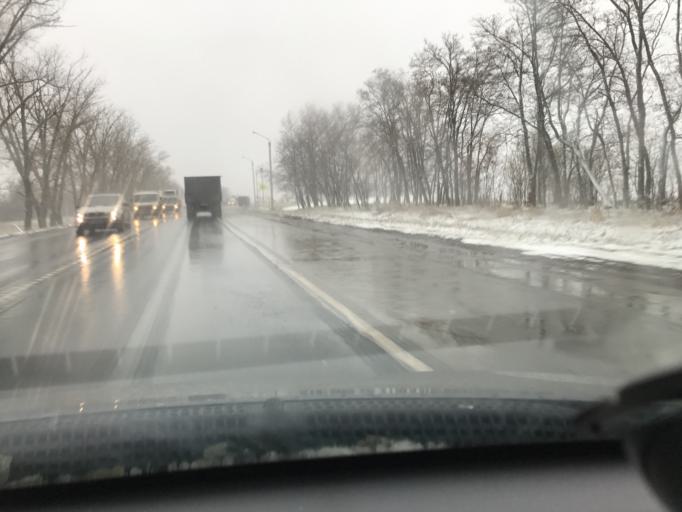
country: RU
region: Rostov
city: Yegorlykskaya
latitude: 46.5895
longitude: 40.6299
